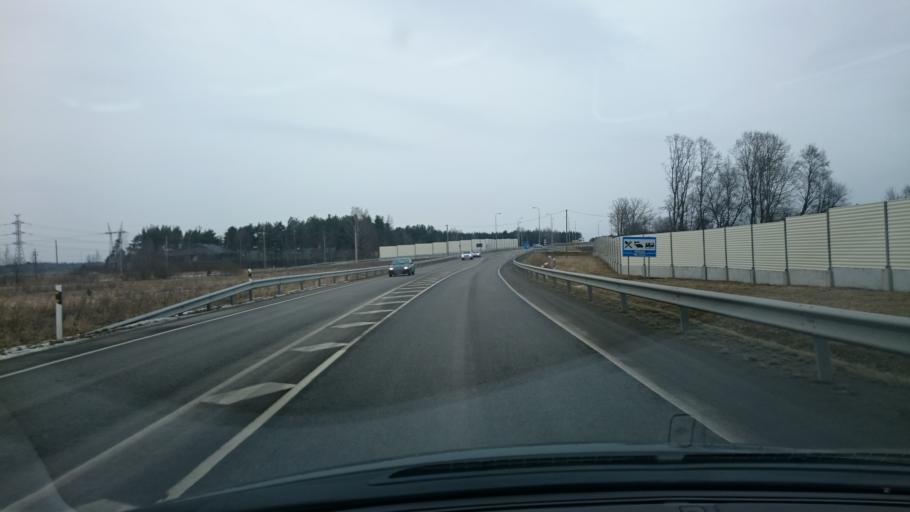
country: EE
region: Harju
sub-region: Saue vald
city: Laagri
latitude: 59.3348
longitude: 24.6160
